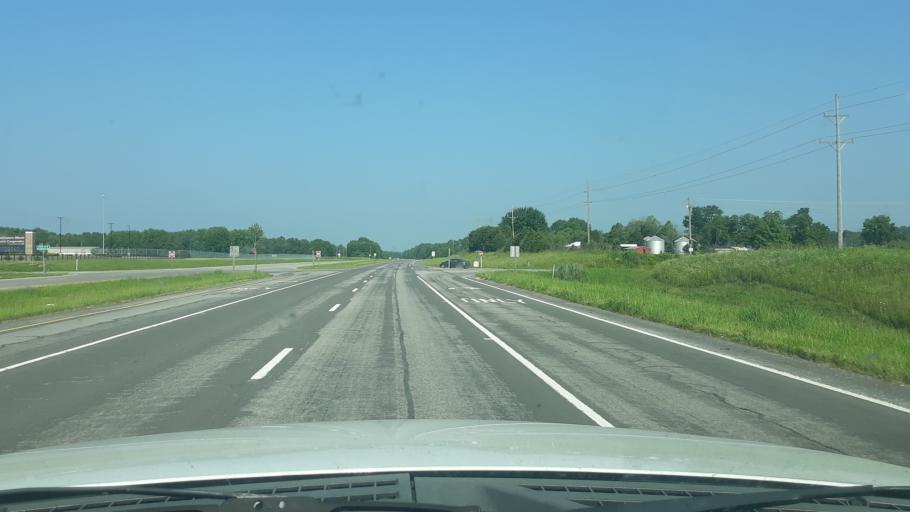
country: US
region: Illinois
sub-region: Saline County
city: Carrier Mills
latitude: 37.7335
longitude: -88.6722
